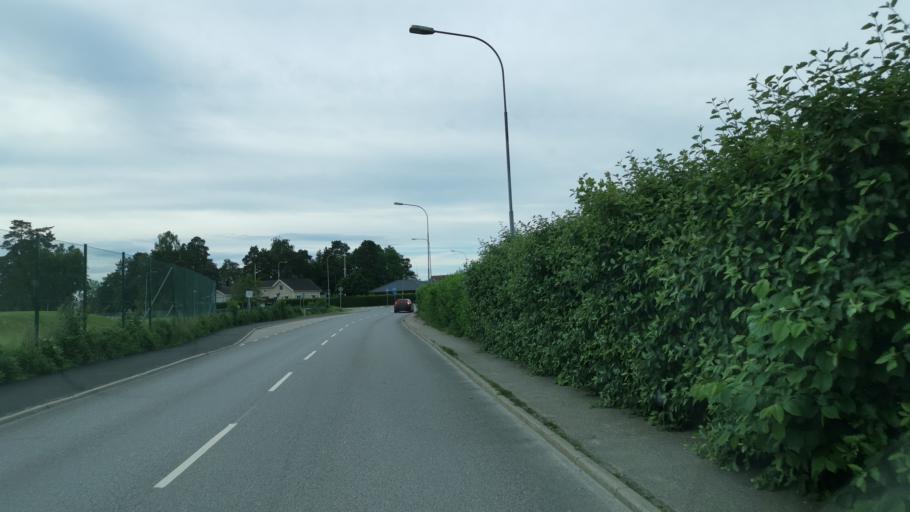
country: SE
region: Vaestra Goetaland
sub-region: Vanersborgs Kommun
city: Vanersborg
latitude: 58.3576
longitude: 12.3527
